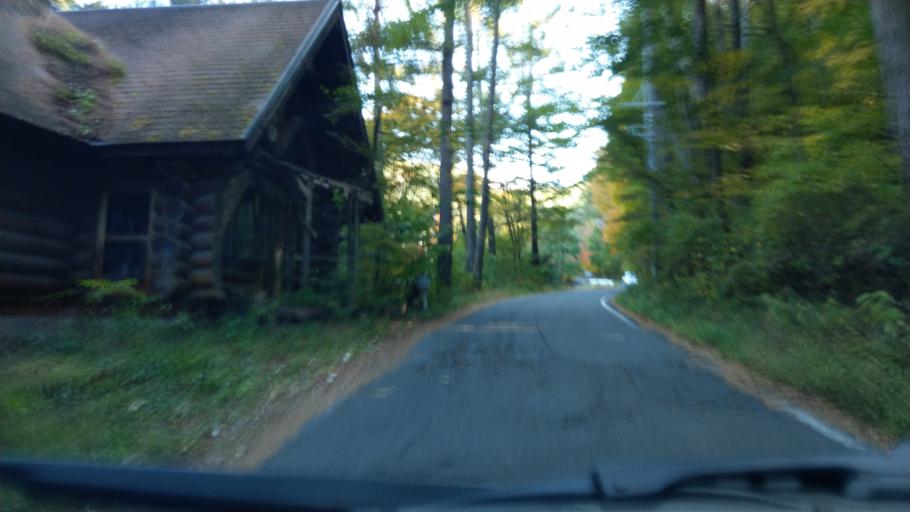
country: JP
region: Nagano
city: Komoro
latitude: 36.3607
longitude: 138.4450
